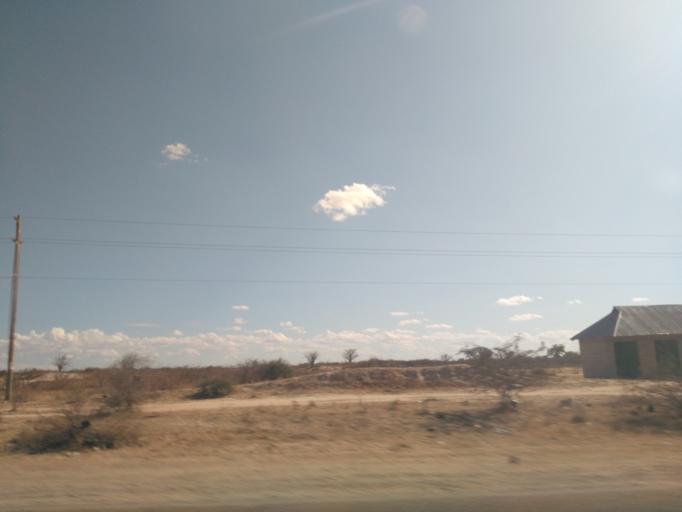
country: TZ
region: Dodoma
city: Dodoma
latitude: -6.1388
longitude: 35.6907
